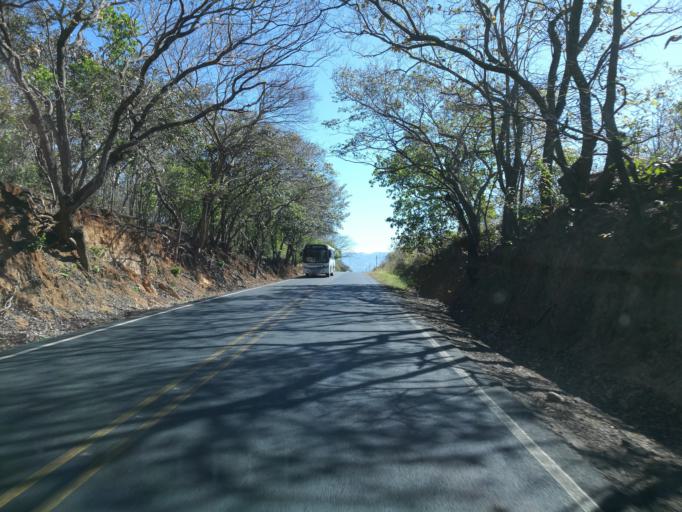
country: CR
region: Puntarenas
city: Miramar
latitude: 10.0879
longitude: -84.8347
